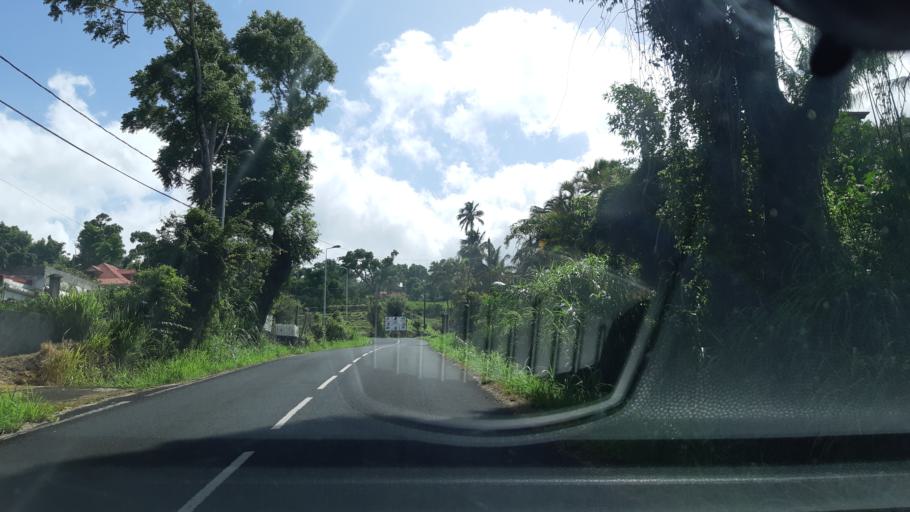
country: GP
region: Guadeloupe
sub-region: Guadeloupe
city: Basse-Terre
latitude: 16.0043
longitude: -61.7148
